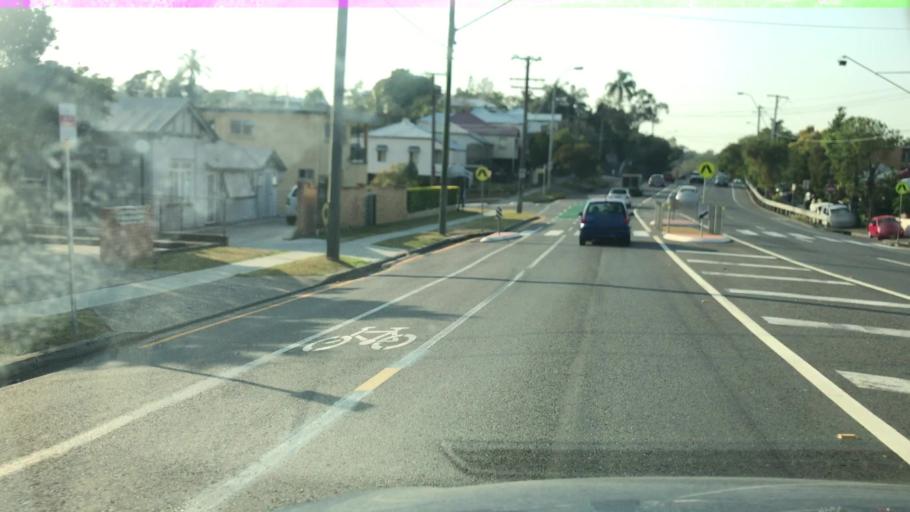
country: AU
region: Queensland
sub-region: Brisbane
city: South Brisbane
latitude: -27.4910
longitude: 153.0194
